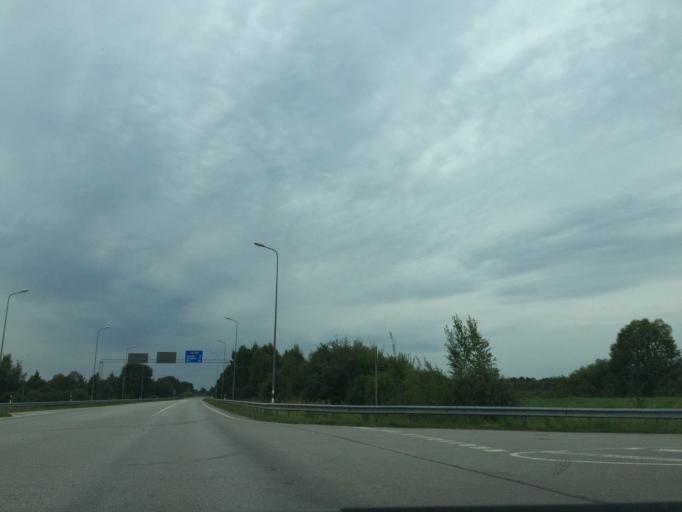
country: LV
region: Cibla
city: Cibla
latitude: 56.4066
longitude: 27.9406
